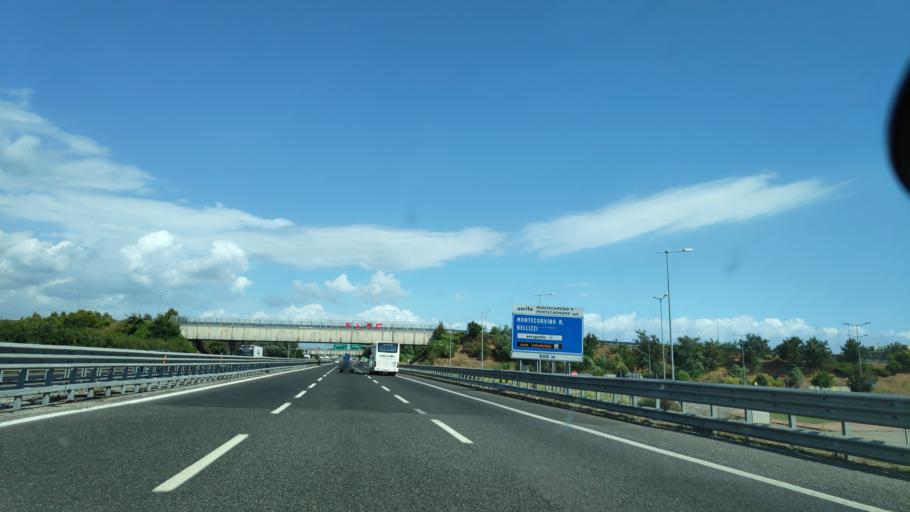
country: IT
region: Campania
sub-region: Provincia di Salerno
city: Pagliarone
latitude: 40.6368
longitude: 14.9091
